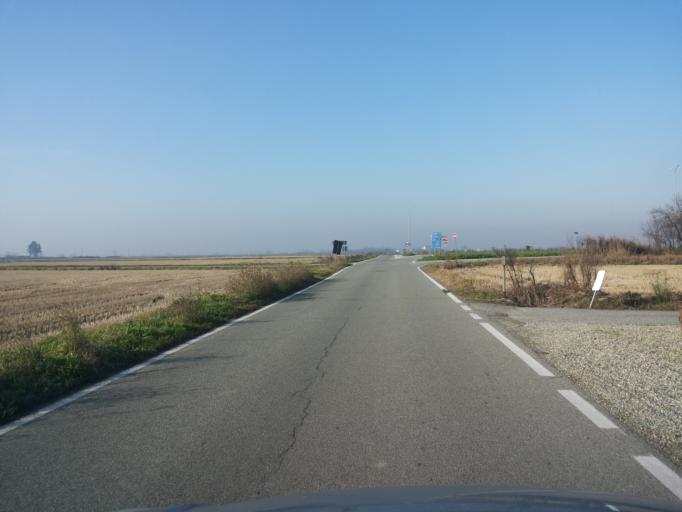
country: IT
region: Piedmont
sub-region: Provincia di Vercelli
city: Stroppiana
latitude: 45.2308
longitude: 8.4466
